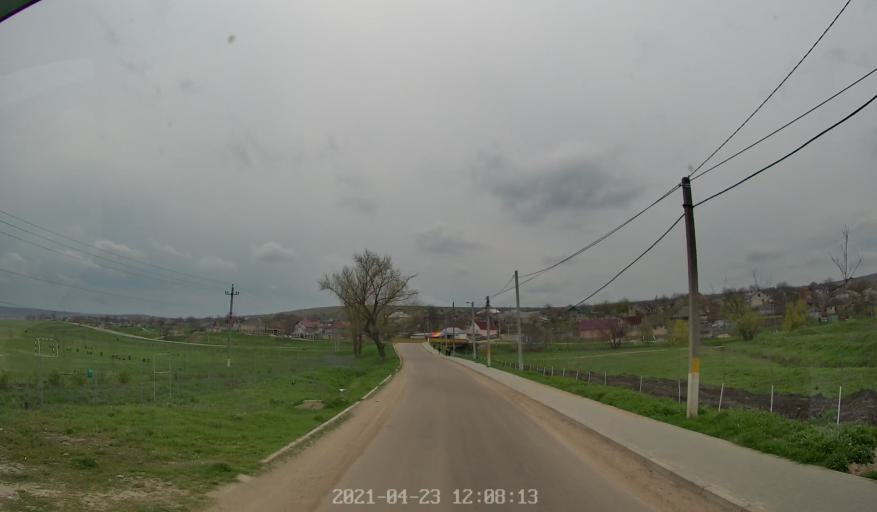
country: MD
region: Chisinau
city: Vadul lui Voda
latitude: 47.1214
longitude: 29.0017
